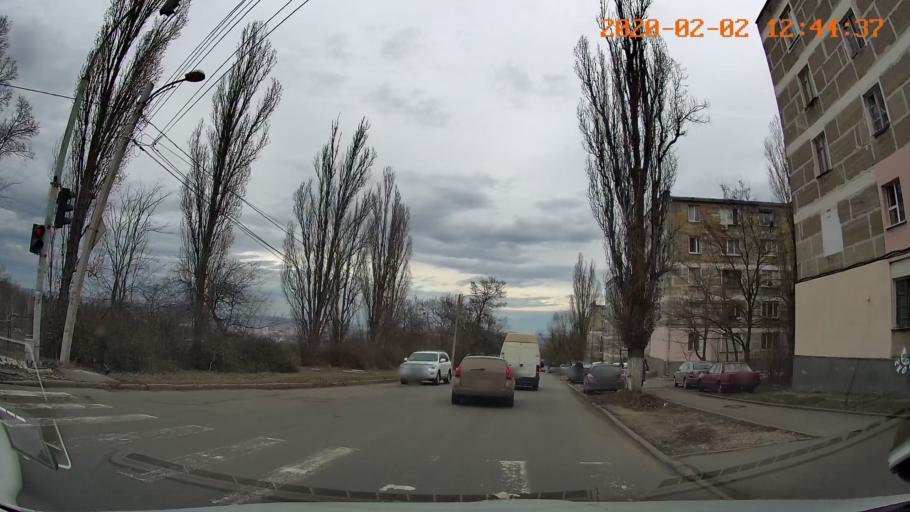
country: MD
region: Chisinau
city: Chisinau
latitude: 47.0030
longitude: 28.8082
